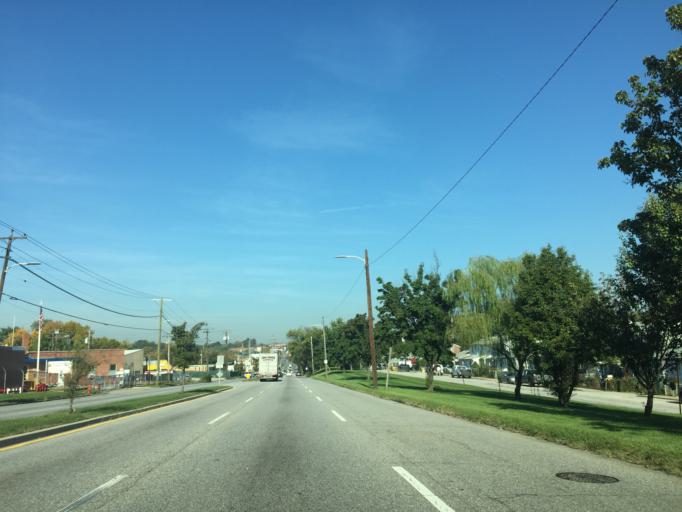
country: US
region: Maryland
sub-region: Baltimore County
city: Rosedale
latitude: 39.3048
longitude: -76.5560
